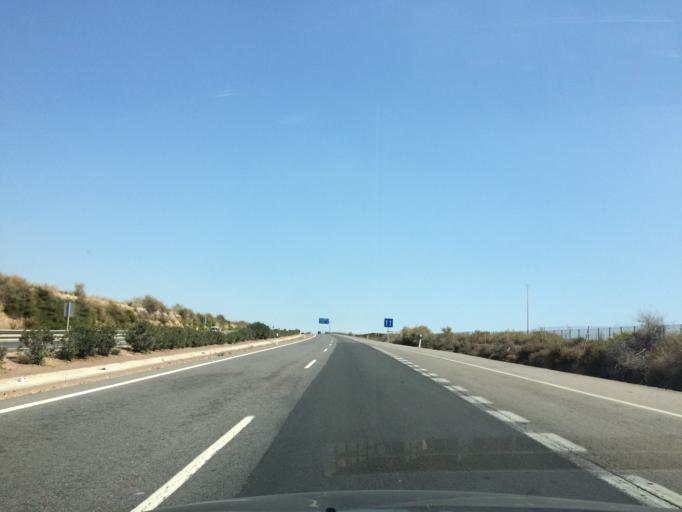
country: ES
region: Andalusia
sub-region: Provincia de Almeria
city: Dalias
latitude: 36.7564
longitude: -2.9136
